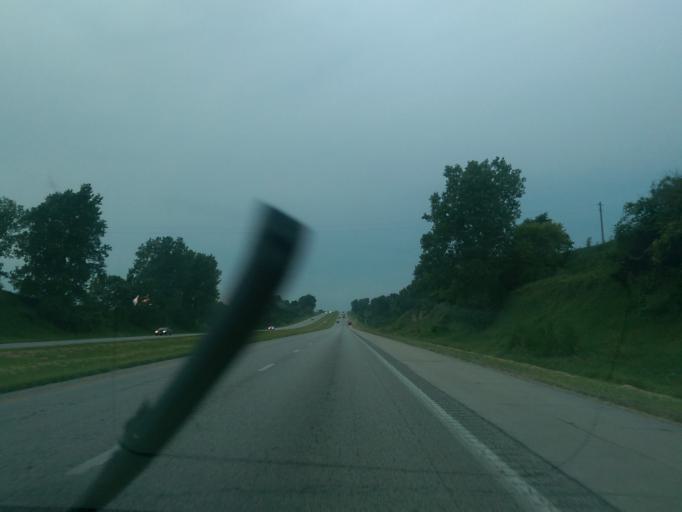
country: US
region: Missouri
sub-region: Holt County
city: Oregon
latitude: 40.0484
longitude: -95.1444
